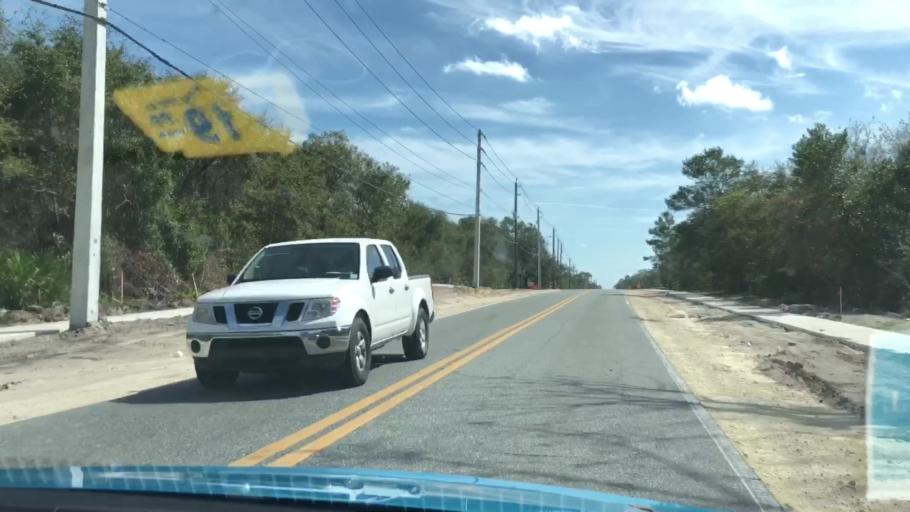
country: US
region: Florida
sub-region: Seminole County
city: Midway
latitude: 28.8593
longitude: -81.1961
